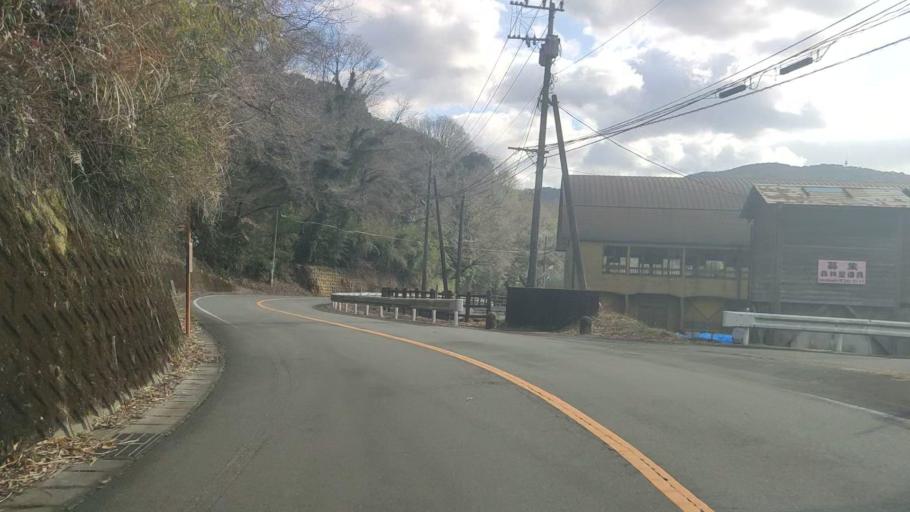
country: JP
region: Kumamoto
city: Hitoyoshi
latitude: 32.2909
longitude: 130.8433
